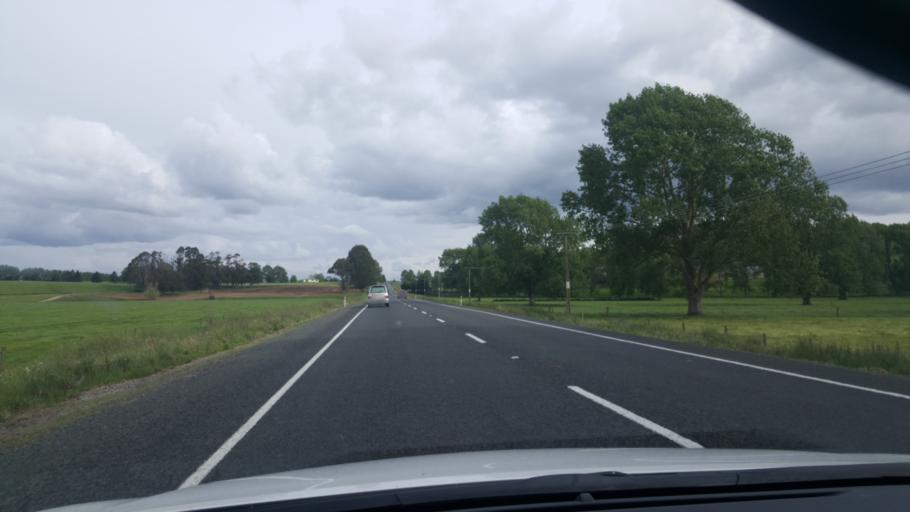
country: NZ
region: Waikato
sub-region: Taupo District
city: Taupo
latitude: -38.4892
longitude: 176.2913
